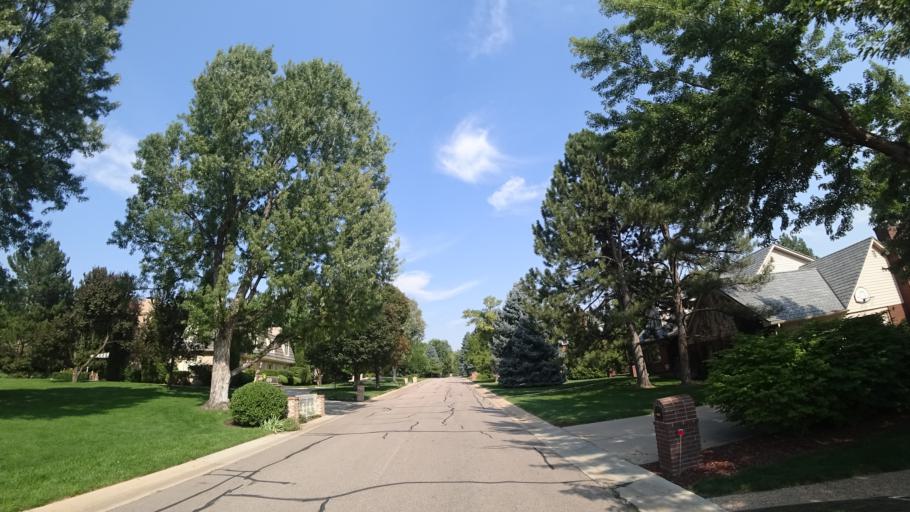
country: US
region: Colorado
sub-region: Arapahoe County
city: Greenwood Village
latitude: 39.6127
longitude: -104.9676
